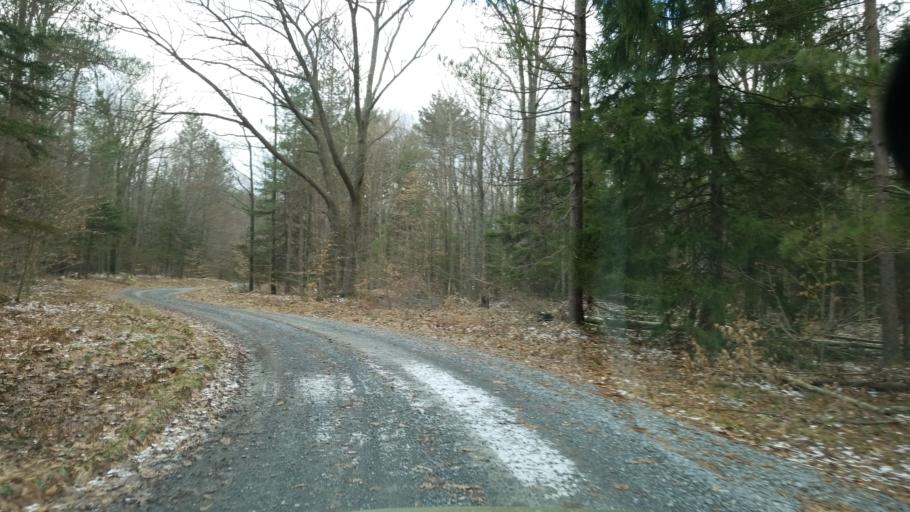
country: US
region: Pennsylvania
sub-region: Clearfield County
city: Clearfield
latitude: 41.1406
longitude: -78.5376
